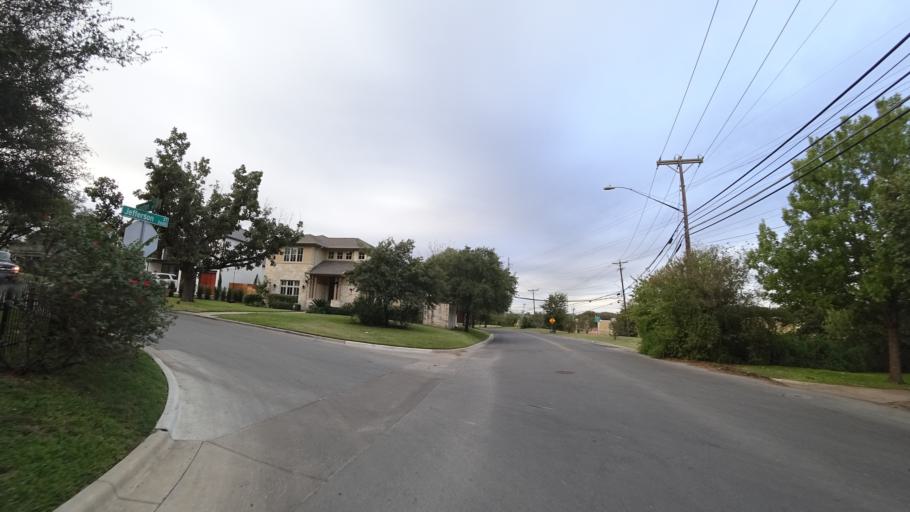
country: US
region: Texas
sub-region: Travis County
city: Austin
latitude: 30.2978
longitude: -97.7576
